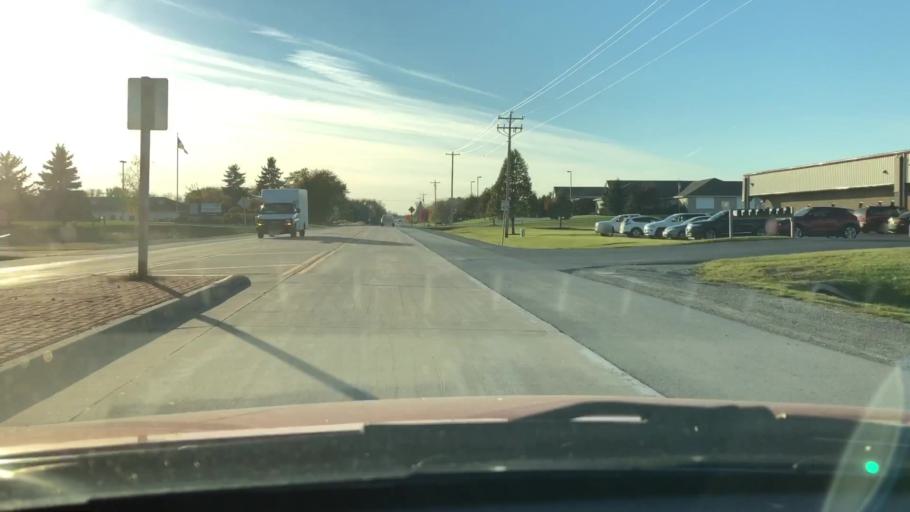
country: US
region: Wisconsin
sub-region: Brown County
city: De Pere
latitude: 44.4303
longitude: -88.1206
